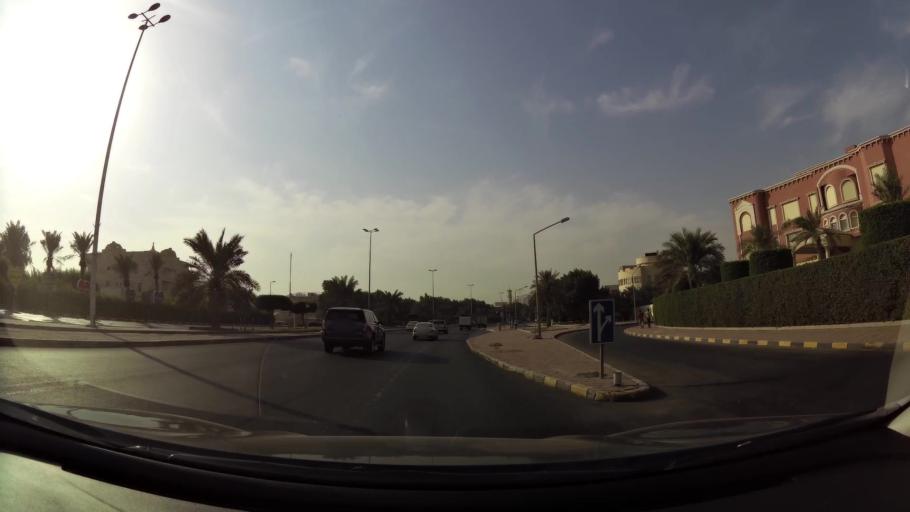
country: KW
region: Muhafazat Hawalli
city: Salwa
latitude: 29.2742
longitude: 48.0888
